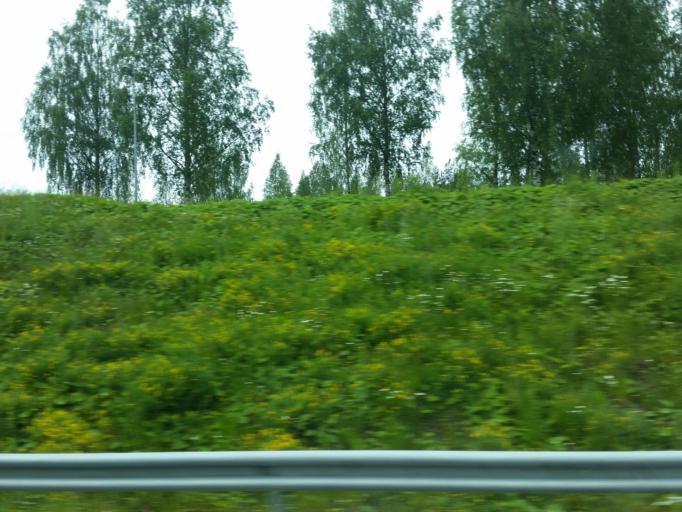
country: FI
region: Northern Savo
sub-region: Kuopio
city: Kuopio
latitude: 62.9589
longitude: 27.6903
